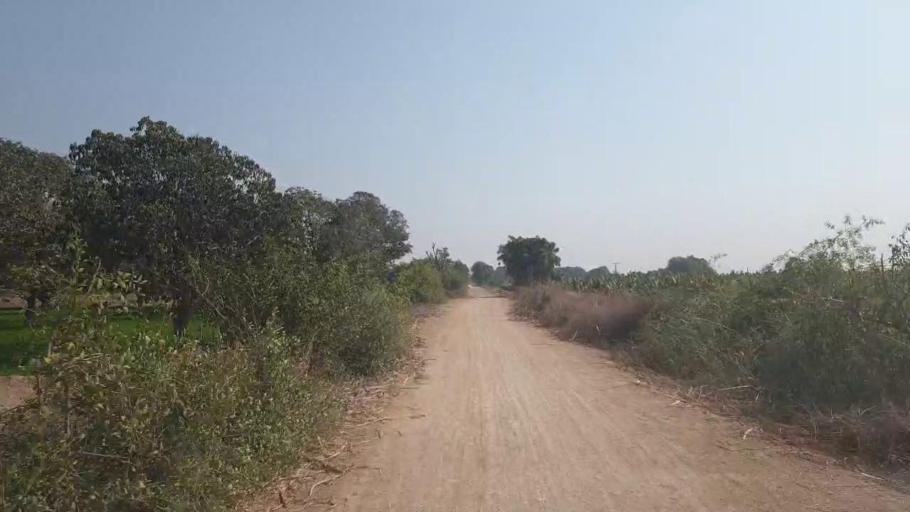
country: PK
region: Sindh
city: Tando Allahyar
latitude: 25.4336
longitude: 68.8422
